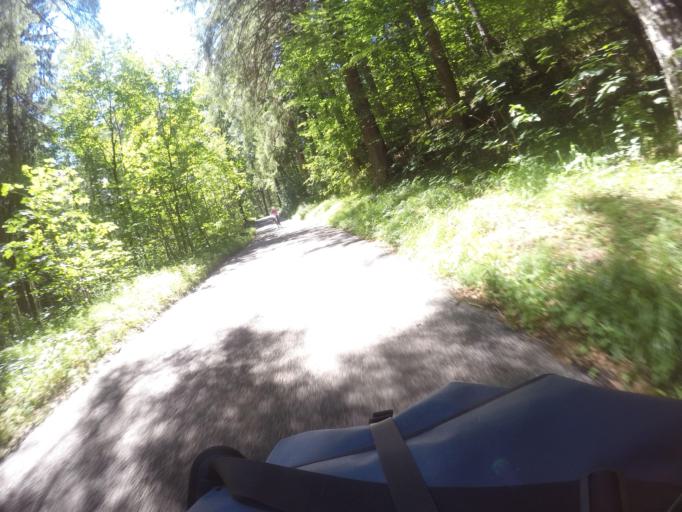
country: AT
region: Tyrol
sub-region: Politischer Bezirk Reutte
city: Musau
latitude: 47.5623
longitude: 10.6696
